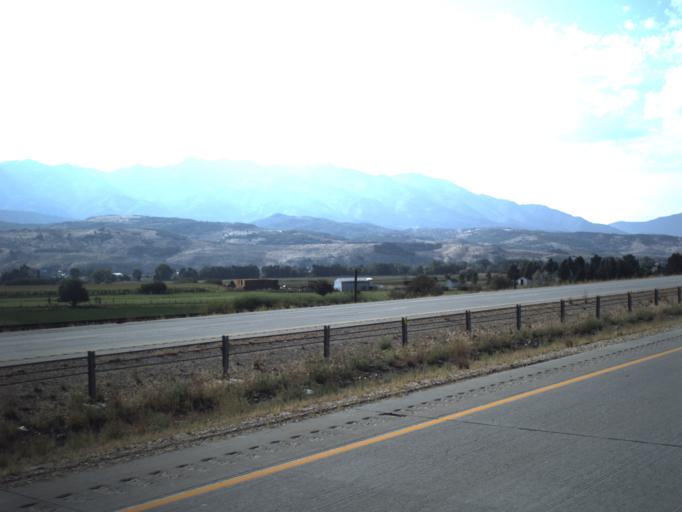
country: US
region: Utah
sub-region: Morgan County
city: Morgan
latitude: 41.0705
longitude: -111.7155
